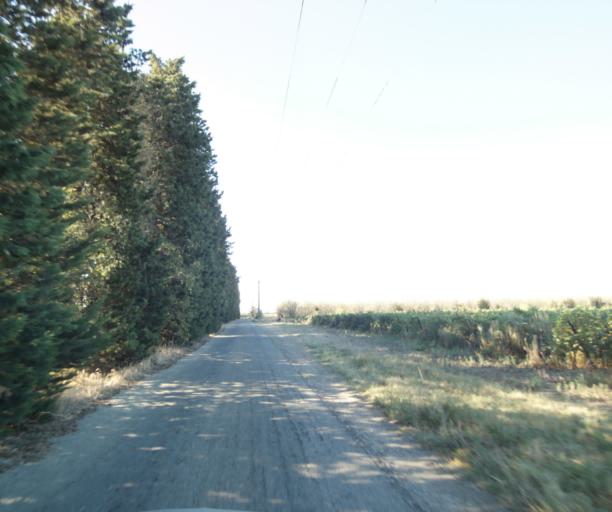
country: FR
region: Languedoc-Roussillon
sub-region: Departement du Gard
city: Manduel
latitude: 43.7853
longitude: 4.4643
